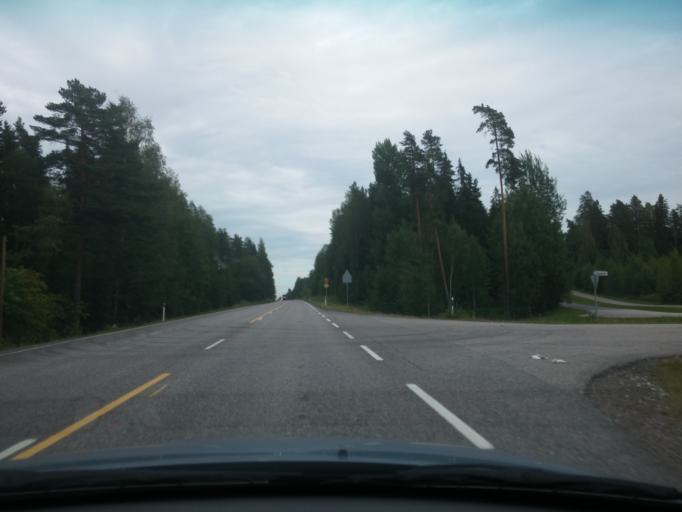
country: FI
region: Haeme
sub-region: Riihimaeki
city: Loppi
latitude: 60.7252
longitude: 24.4134
